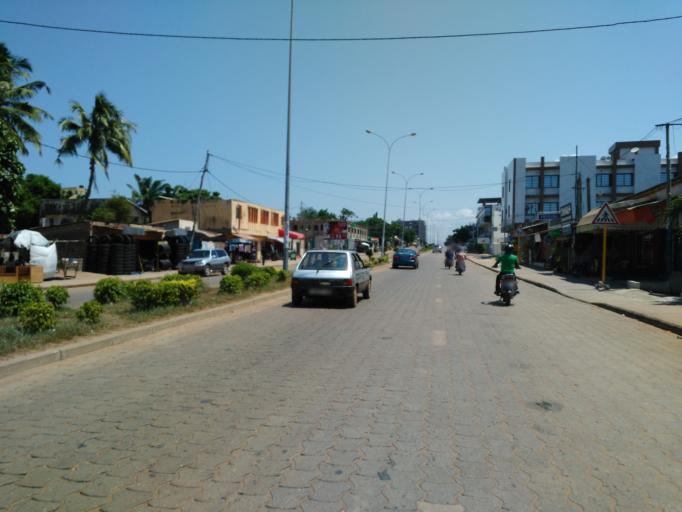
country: TG
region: Maritime
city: Lome
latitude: 6.1649
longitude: 1.2213
